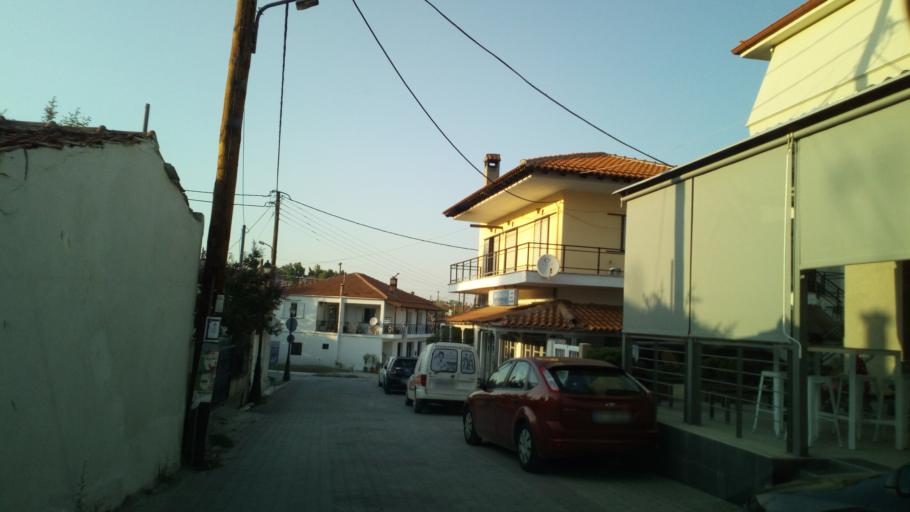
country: GR
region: Central Macedonia
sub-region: Nomos Chalkidikis
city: Pefkochori
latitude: 39.9418
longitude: 23.6632
